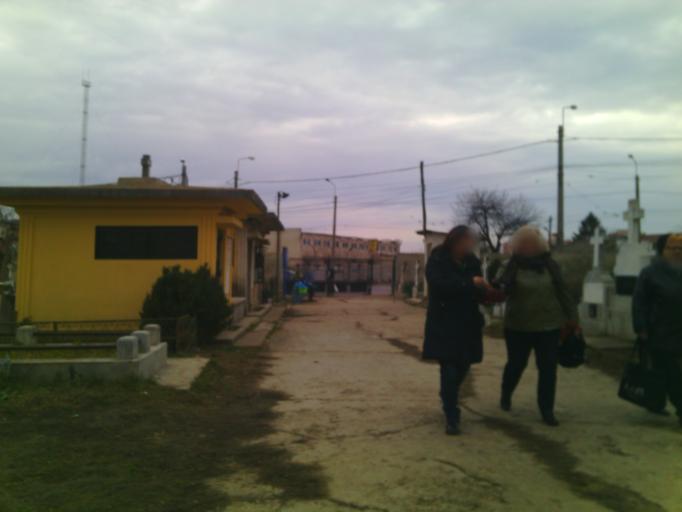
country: RO
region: Ilfov
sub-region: Comuna Jilava
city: Jilava
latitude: 44.3811
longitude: 26.0847
